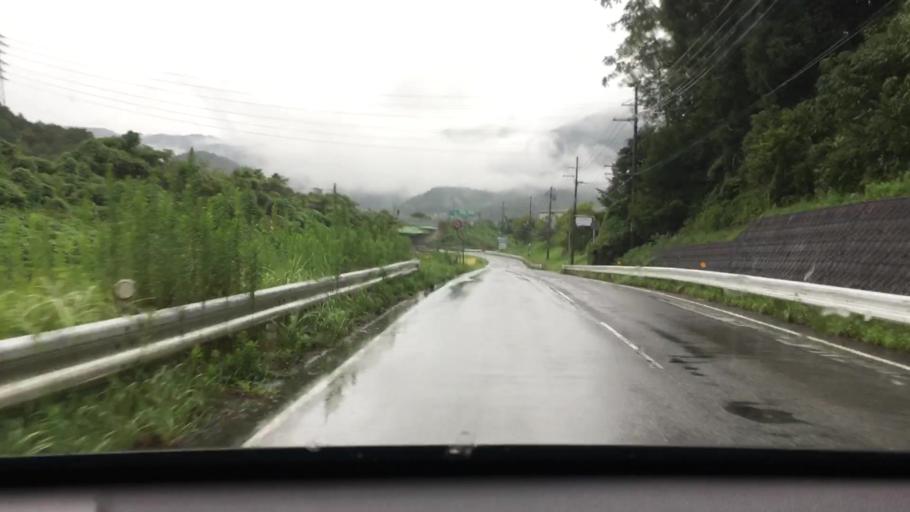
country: JP
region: Hyogo
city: Toyooka
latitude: 35.3115
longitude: 134.8548
